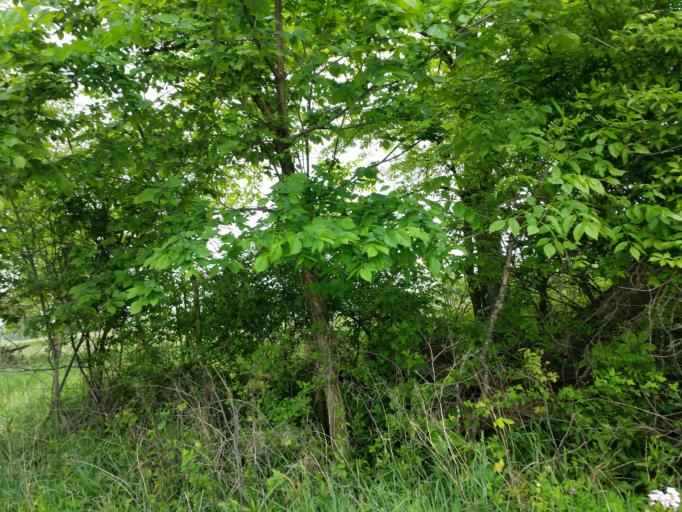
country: US
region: Michigan
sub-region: Eaton County
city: Waverly
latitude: 42.7698
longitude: -84.6389
